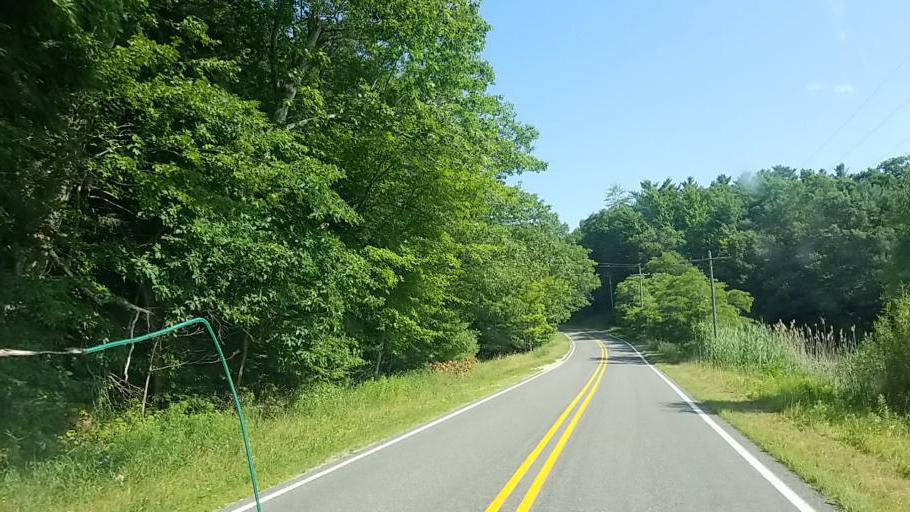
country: US
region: Michigan
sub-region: Muskegon County
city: Whitehall
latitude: 43.3287
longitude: -86.3995
